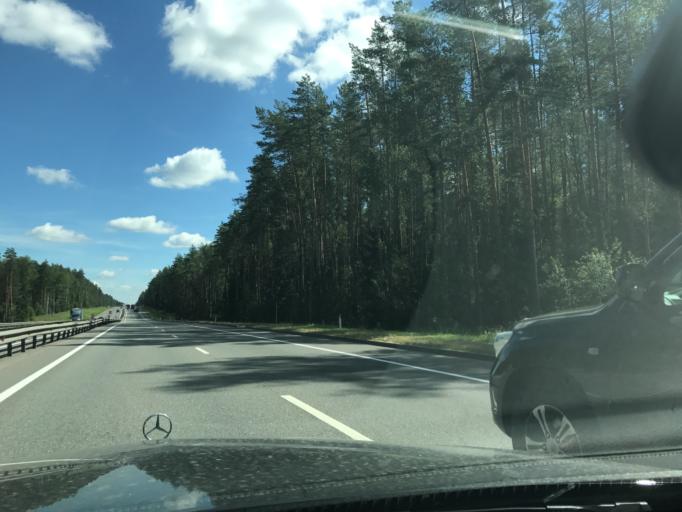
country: RU
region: Vladimir
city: Stepantsevo
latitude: 56.2237
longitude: 41.5814
